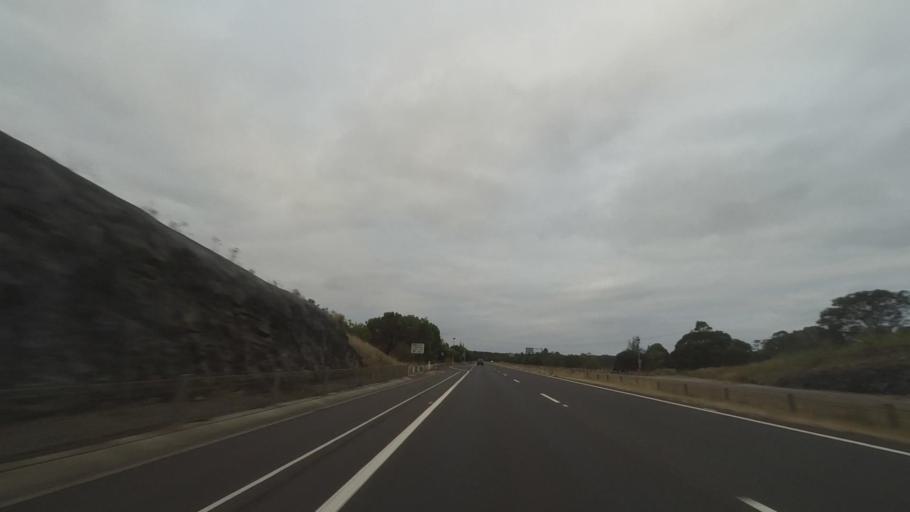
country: AU
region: New South Wales
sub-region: Shellharbour
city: Croom
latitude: -34.6215
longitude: 150.8374
